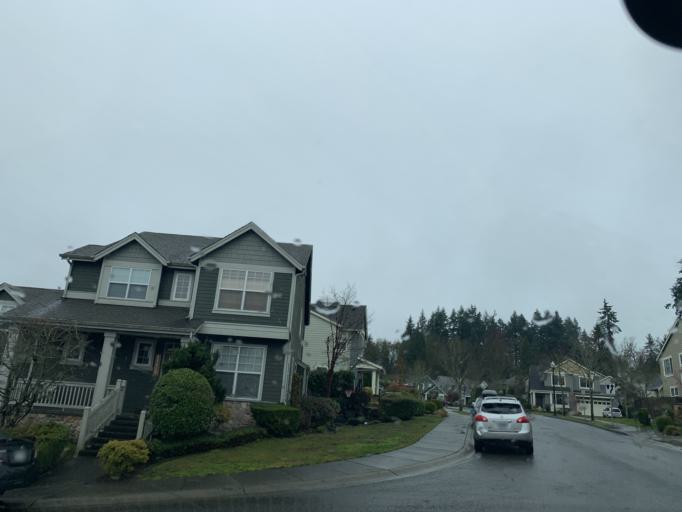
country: US
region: Washington
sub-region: King County
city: Woodinville
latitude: 47.7405
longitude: -122.1677
